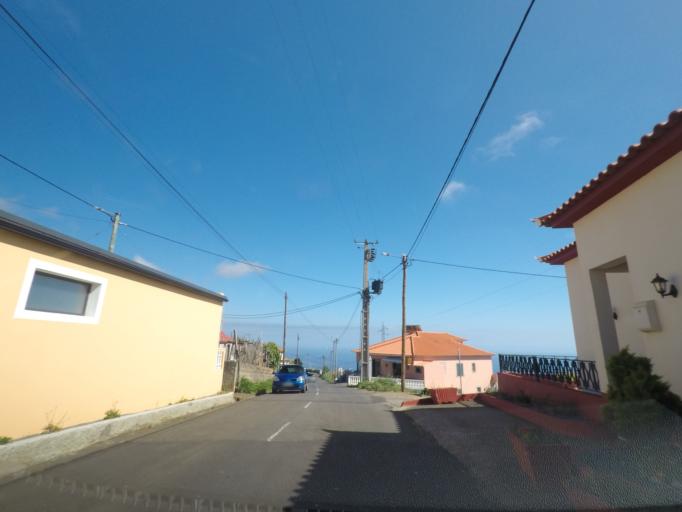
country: PT
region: Madeira
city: Ponta do Sol
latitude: 32.6978
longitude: -17.1055
